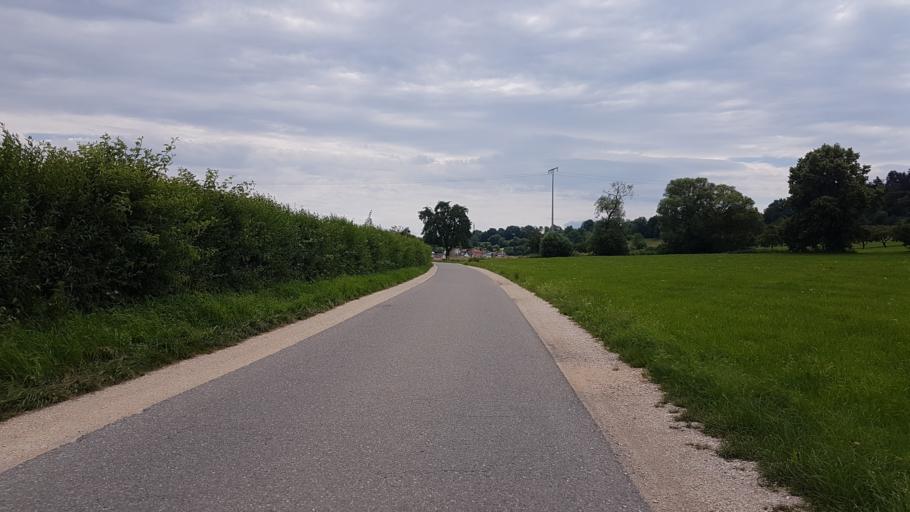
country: DE
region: Baden-Wuerttemberg
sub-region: Tuebingen Region
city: Scheer
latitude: 48.0599
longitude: 9.3007
